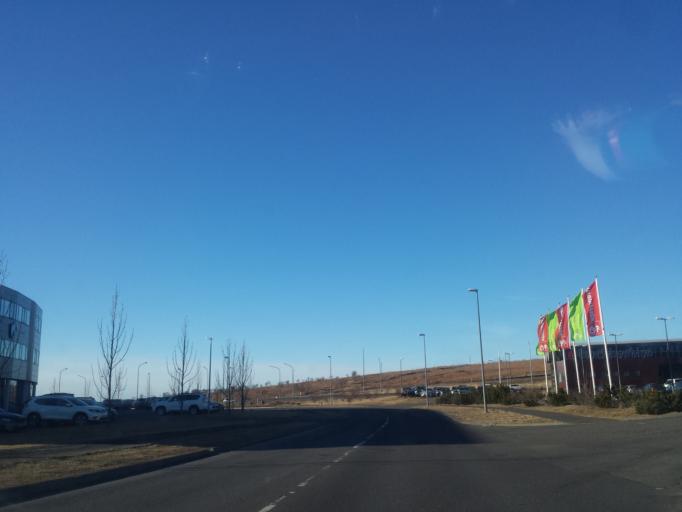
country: IS
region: Capital Region
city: Mosfellsbaer
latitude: 64.1303
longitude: -21.7631
